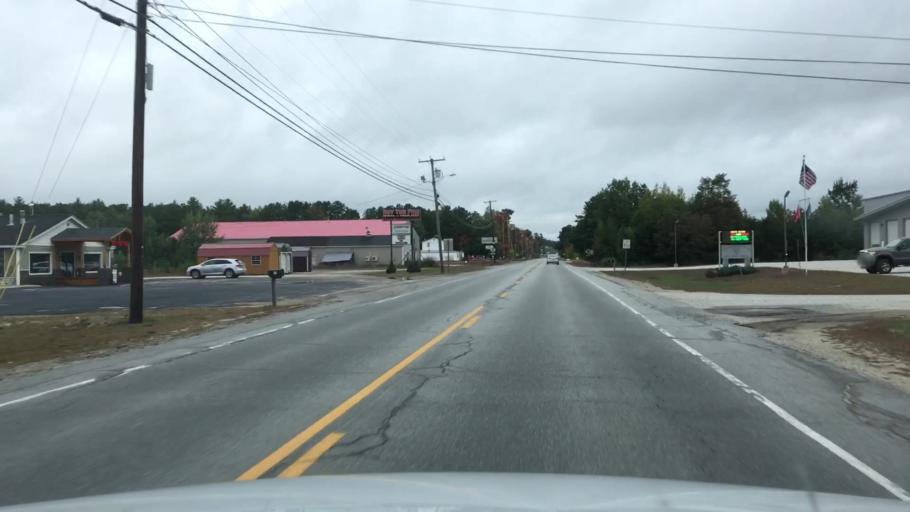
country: US
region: Maine
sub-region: Oxford County
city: Oxford
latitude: 44.1451
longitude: -70.4785
